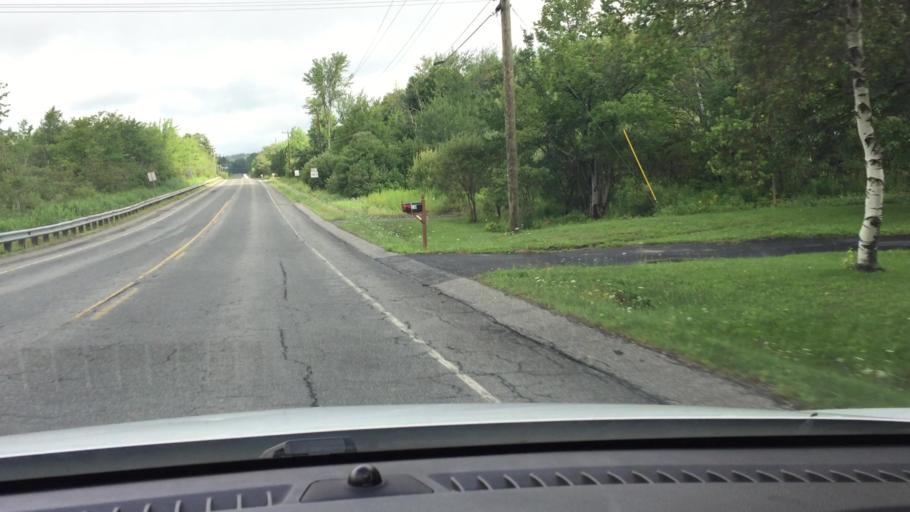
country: US
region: Massachusetts
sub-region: Berkshire County
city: Hinsdale
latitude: 42.4387
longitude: -73.0474
